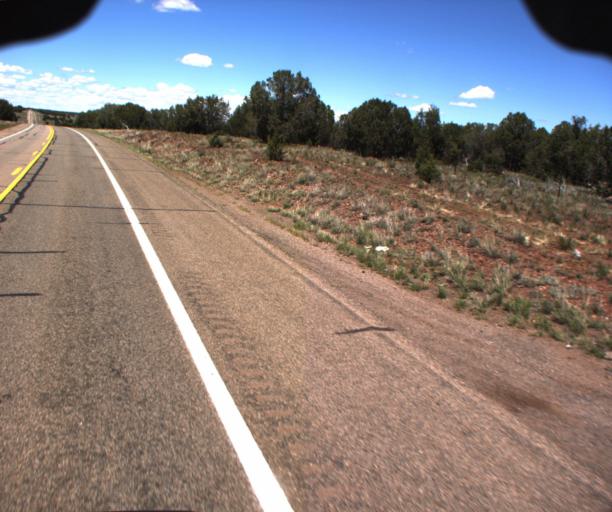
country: US
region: Arizona
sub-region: Yavapai County
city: Paulden
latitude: 35.1368
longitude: -112.4414
